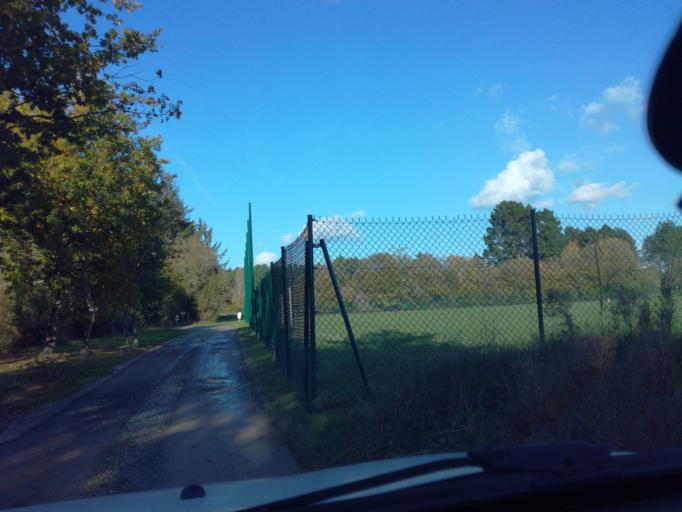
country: FR
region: Brittany
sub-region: Departement d'Ille-et-Vilaine
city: Bruz
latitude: 48.0308
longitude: -1.7704
